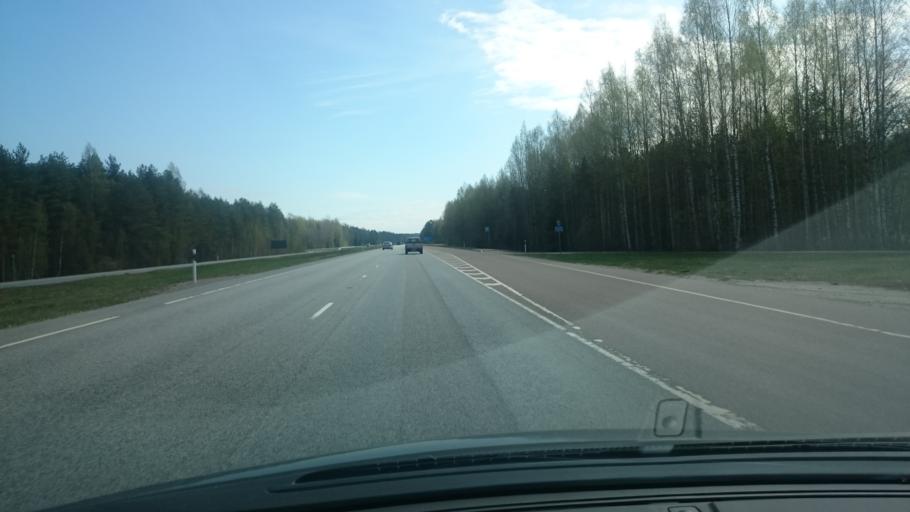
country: EE
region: Harju
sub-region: Kuusalu vald
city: Kuusalu
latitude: 59.4603
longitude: 25.5900
